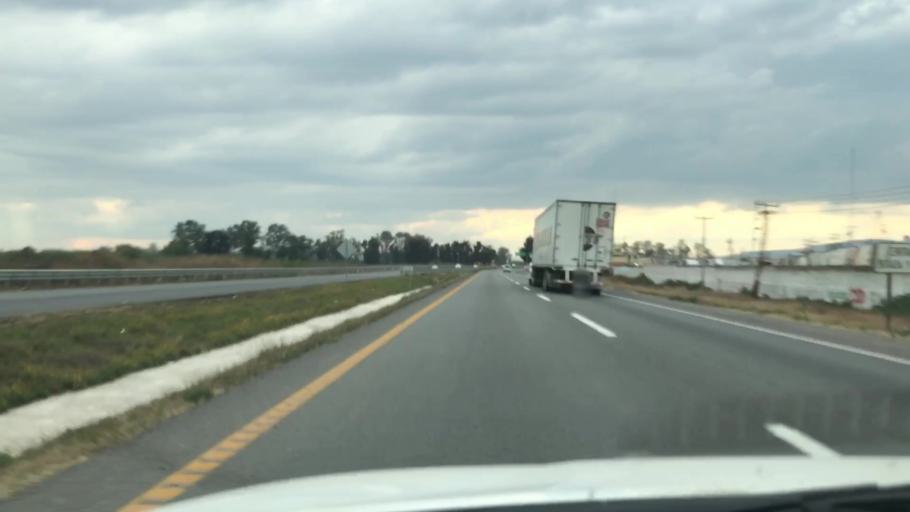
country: MX
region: Guanajuato
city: Irapuato
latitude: 20.6495
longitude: -101.3486
